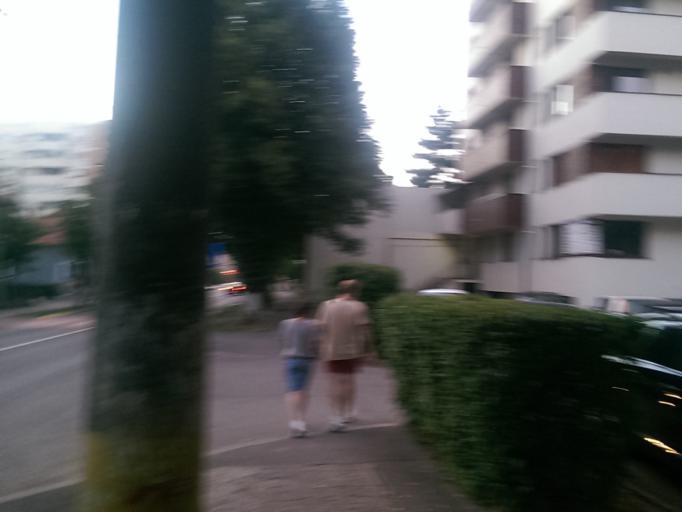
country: RO
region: Cluj
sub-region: Municipiul Cluj-Napoca
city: Cluj-Napoca
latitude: 46.7666
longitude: 23.6198
